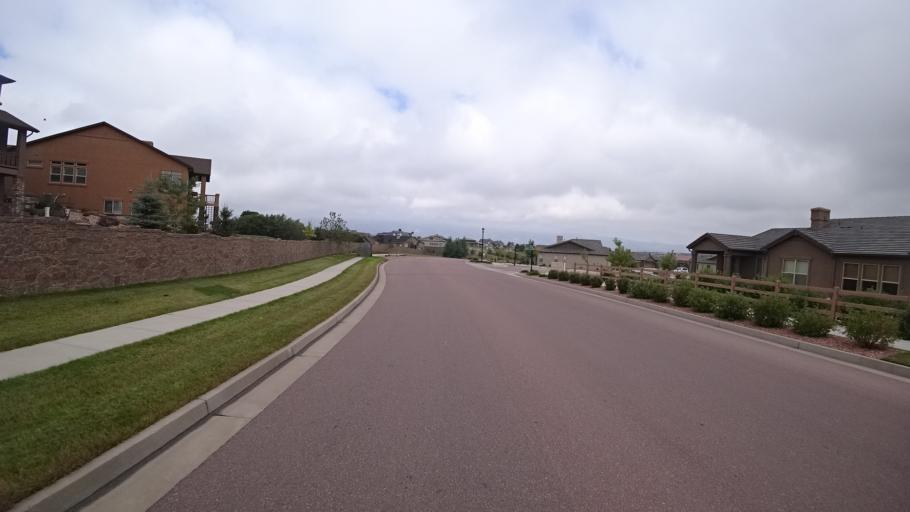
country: US
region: Colorado
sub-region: El Paso County
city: Gleneagle
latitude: 39.0155
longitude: -104.7877
